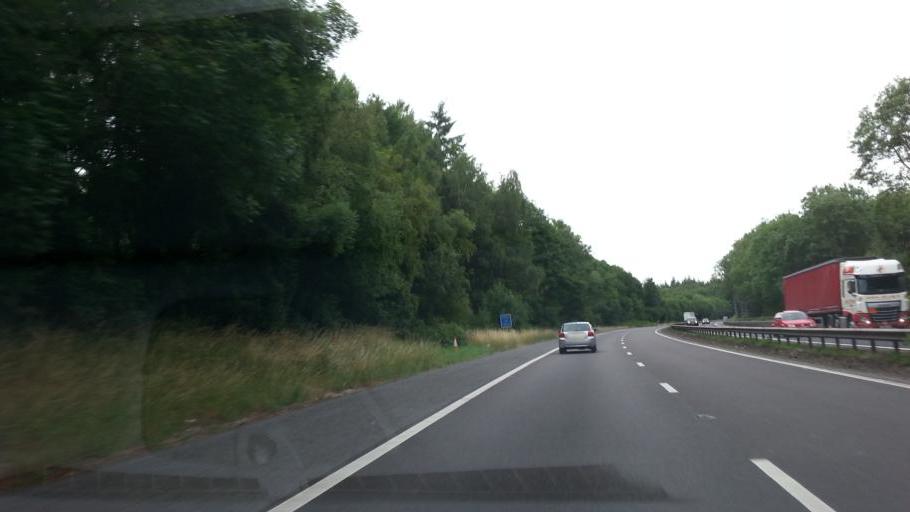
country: GB
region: England
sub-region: Herefordshire
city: Linton
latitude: 51.9379
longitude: -2.4781
